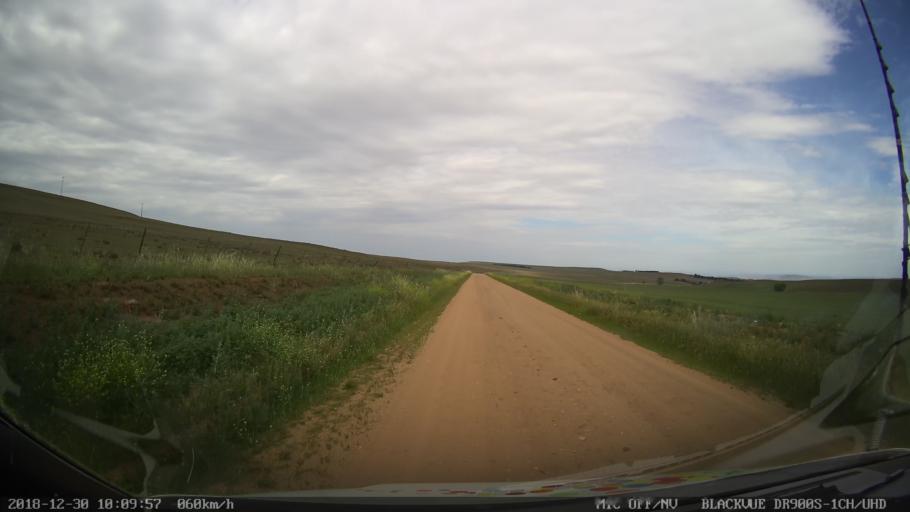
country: AU
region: New South Wales
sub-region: Cooma-Monaro
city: Cooma
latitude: -36.5499
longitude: 149.1002
